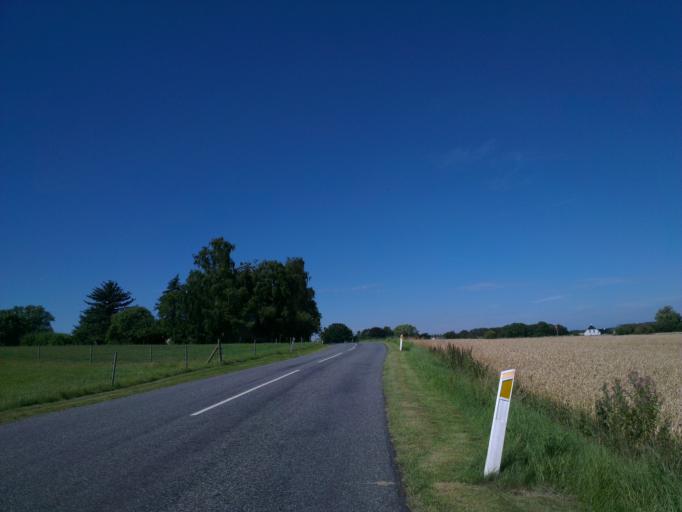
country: DK
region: Capital Region
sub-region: Frederikssund Kommune
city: Frederikssund
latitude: 55.8715
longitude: 12.0861
